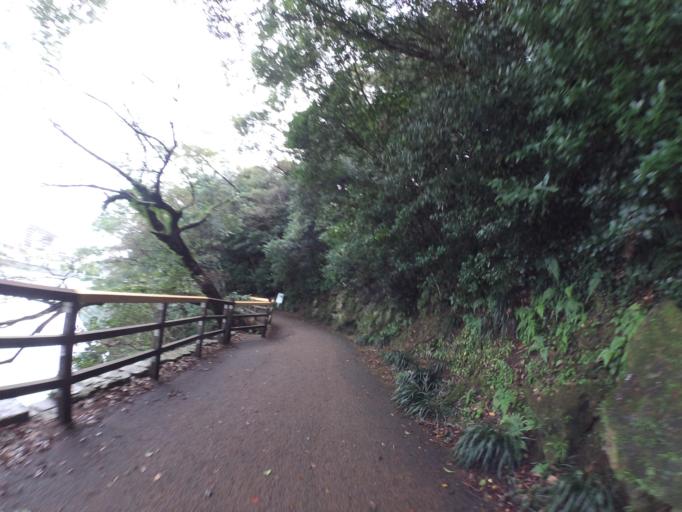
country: JP
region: Tokushima
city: Tokushima-shi
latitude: 34.0764
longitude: 134.5552
